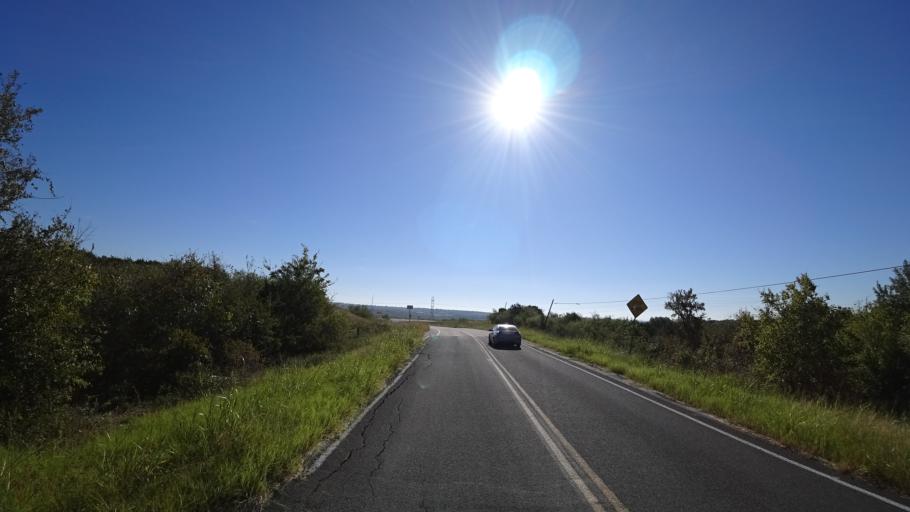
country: US
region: Texas
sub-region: Travis County
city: Manor
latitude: 30.2997
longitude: -97.5728
